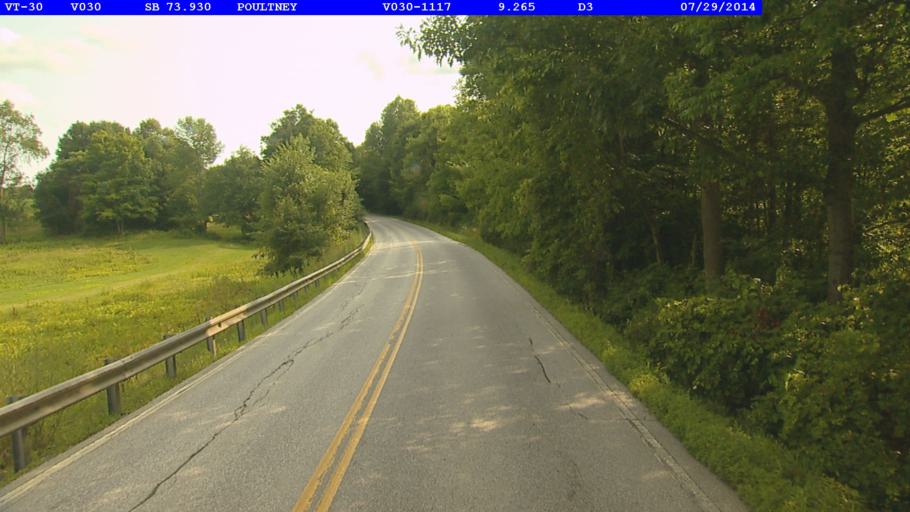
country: US
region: Vermont
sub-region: Rutland County
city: Castleton
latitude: 43.5825
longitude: -73.2141
